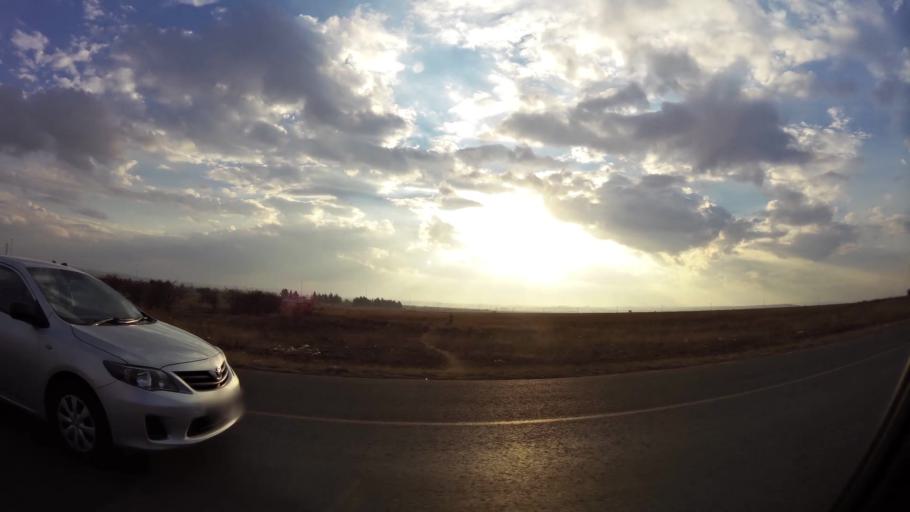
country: ZA
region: Gauteng
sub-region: Sedibeng District Municipality
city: Vanderbijlpark
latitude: -26.5996
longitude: 27.8186
